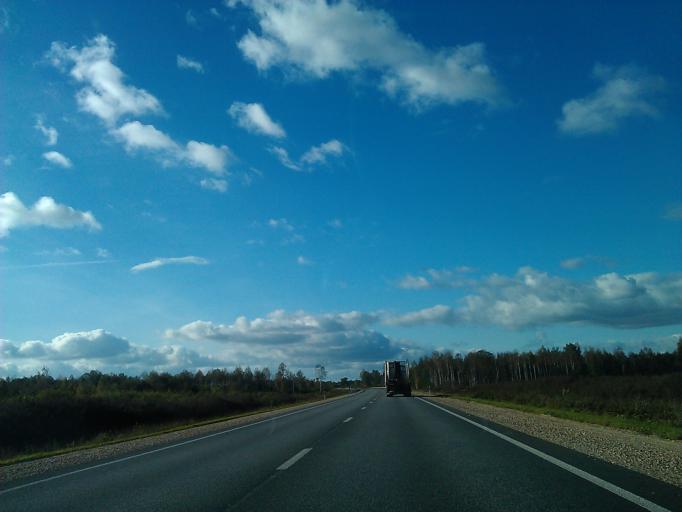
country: LV
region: Koknese
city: Koknese
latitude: 56.6890
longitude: 25.3665
